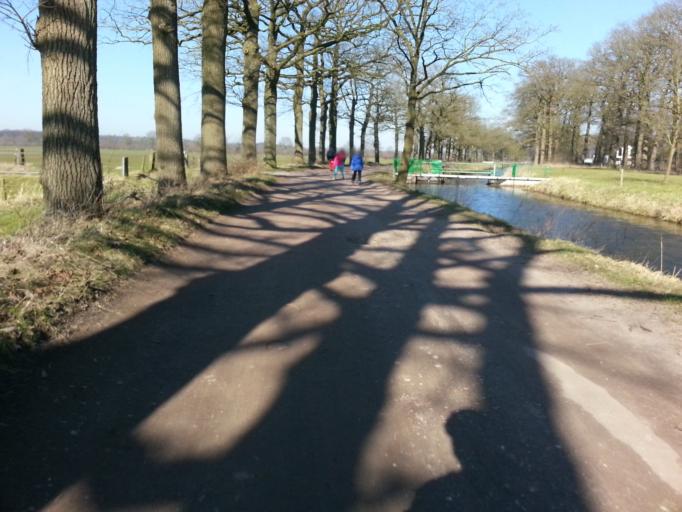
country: NL
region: Utrecht
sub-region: Gemeente Woudenberg
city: Woudenberg
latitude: 52.0911
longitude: 5.4008
